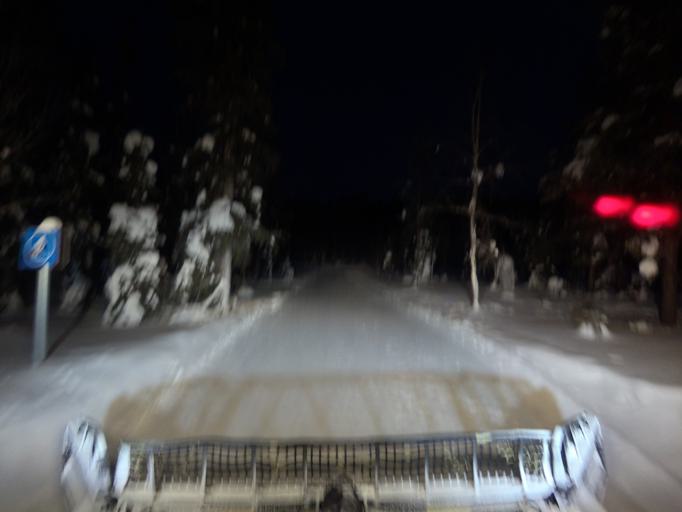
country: FI
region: Lapland
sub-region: Tunturi-Lappi
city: Kolari
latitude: 67.5810
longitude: 24.0796
